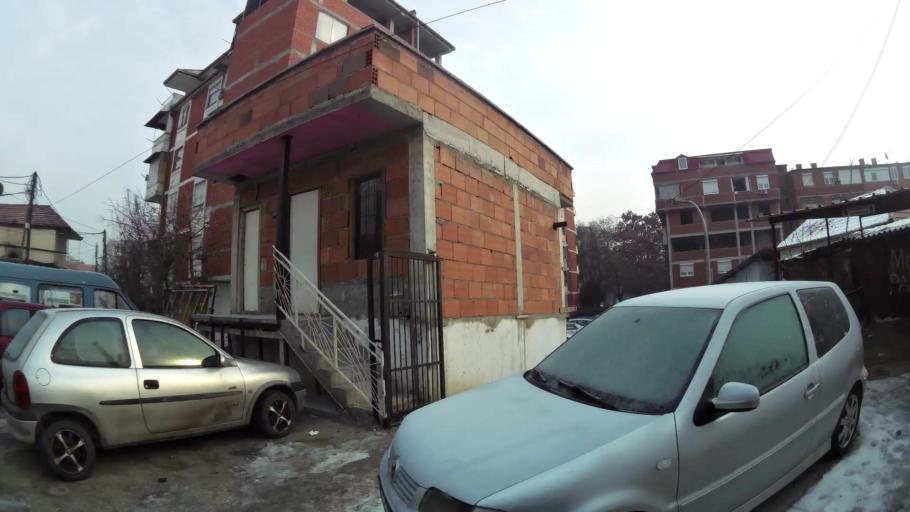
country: MK
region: Cair
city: Cair
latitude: 42.0175
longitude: 21.4391
